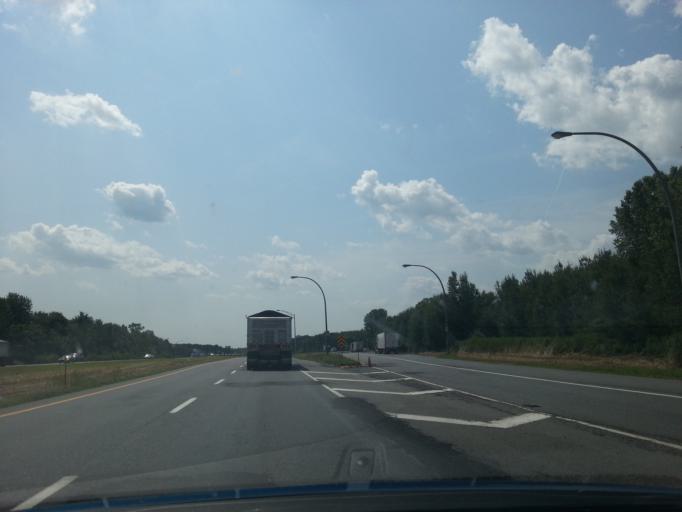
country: CA
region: Quebec
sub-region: Monteregie
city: Beloeil
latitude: 45.6022
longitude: -73.1168
